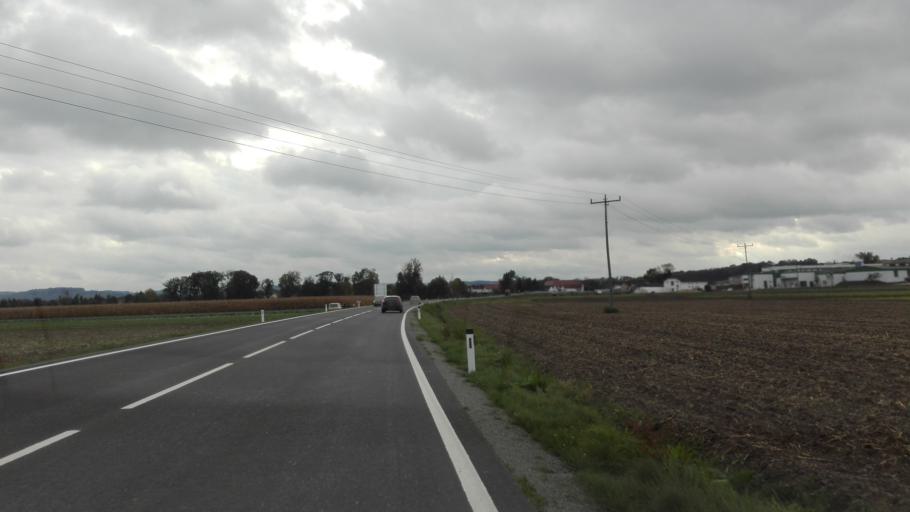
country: AT
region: Upper Austria
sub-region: Politischer Bezirk Urfahr-Umgebung
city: Feldkirchen an der Donau
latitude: 48.3159
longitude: 14.0073
